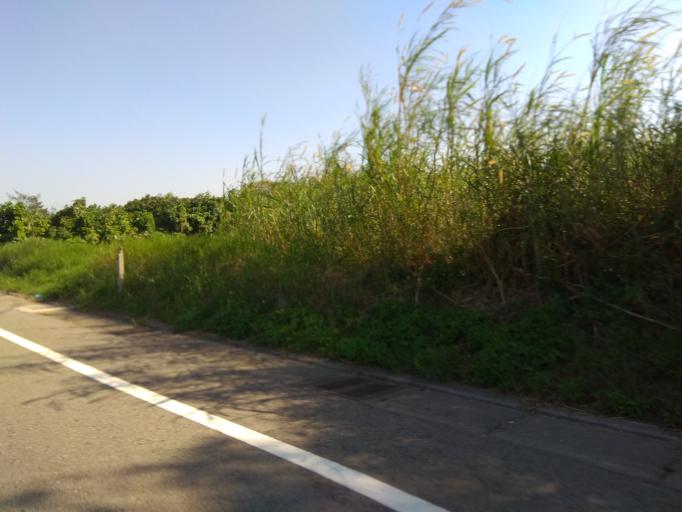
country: TW
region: Taiwan
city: Taoyuan City
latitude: 25.0350
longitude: 121.1060
